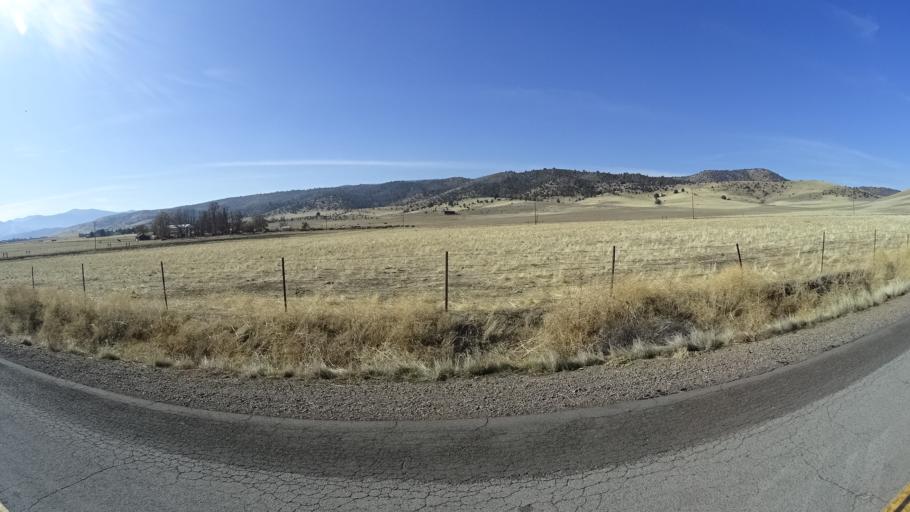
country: US
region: California
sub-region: Siskiyou County
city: Montague
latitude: 41.5984
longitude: -122.5347
